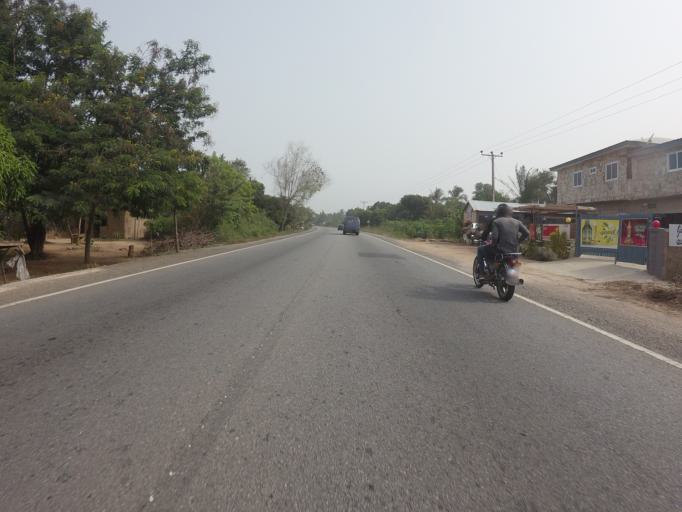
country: GH
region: Volta
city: Anloga
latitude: 5.9949
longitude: 0.5663
